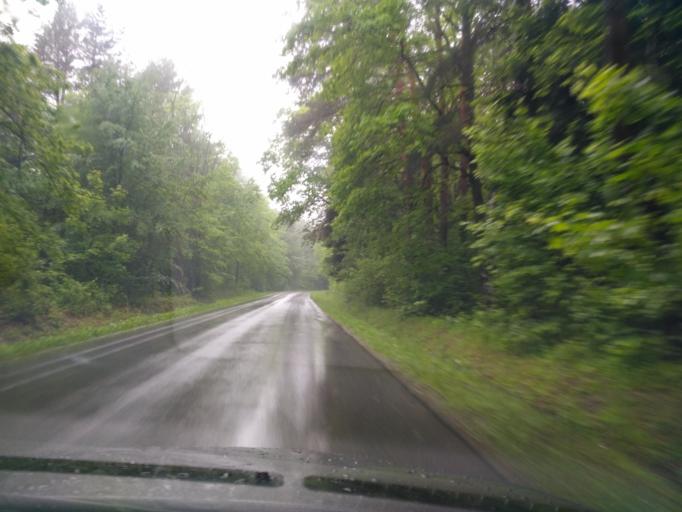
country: PL
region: Subcarpathian Voivodeship
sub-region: Powiat jasielski
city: Debowiec
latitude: 49.6613
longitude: 21.4330
